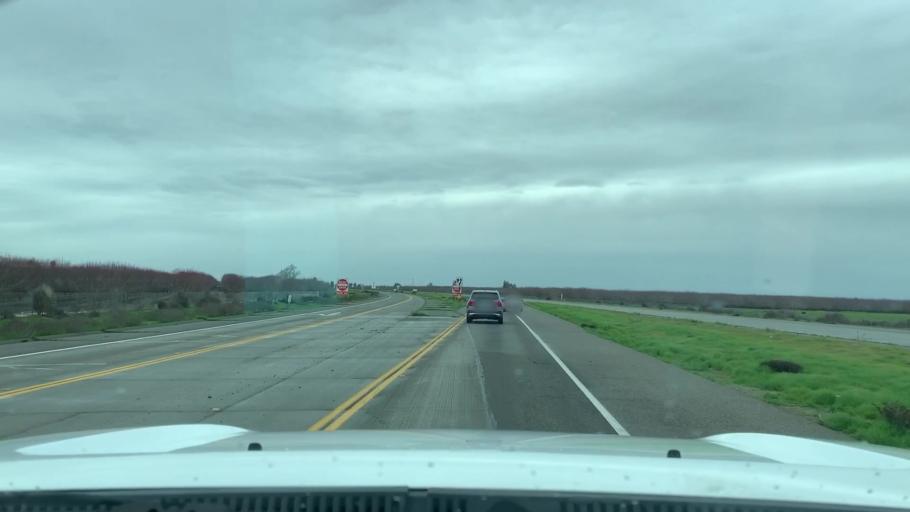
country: US
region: California
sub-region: Fresno County
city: Caruthers
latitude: 36.4944
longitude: -119.7873
